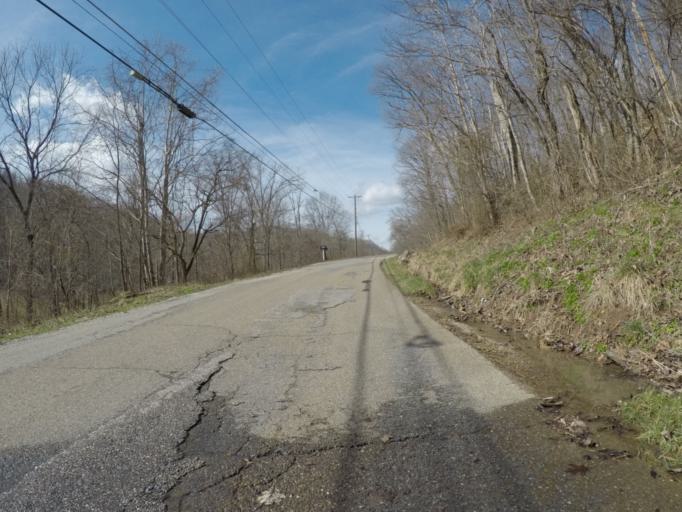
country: US
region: Ohio
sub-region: Lawrence County
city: Burlington
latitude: 38.4782
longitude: -82.4996
